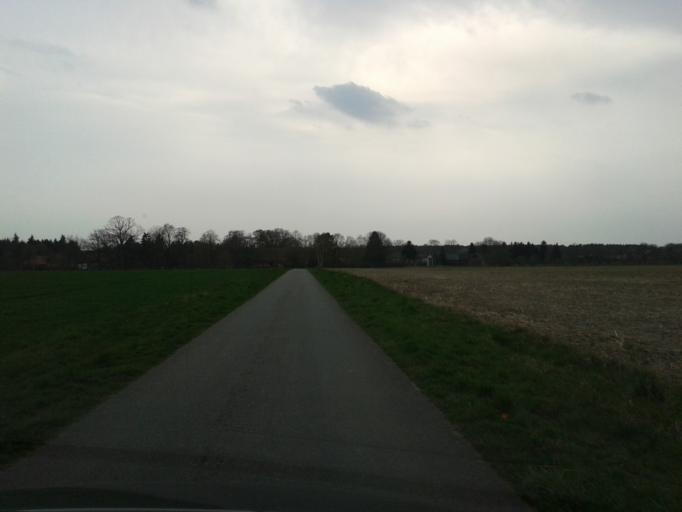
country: DE
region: Lower Saxony
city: Woltersdorf
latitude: 52.9211
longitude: 11.2361
